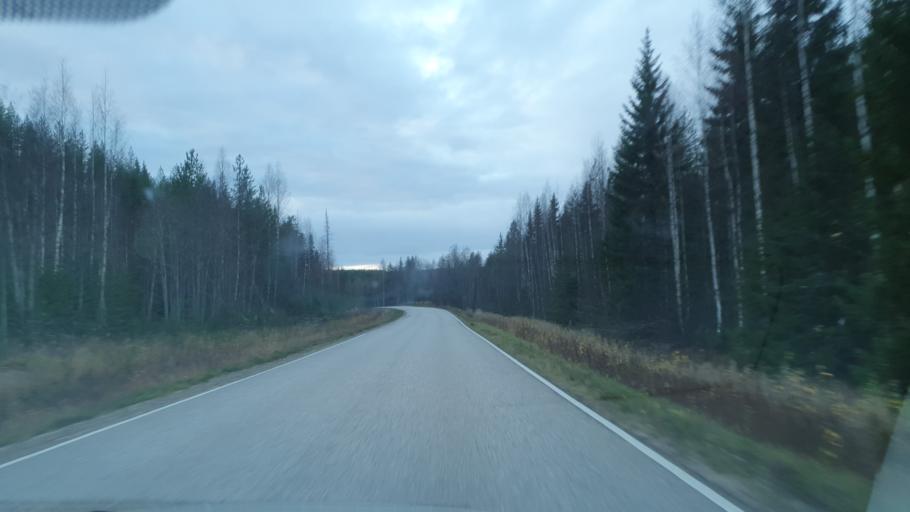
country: FI
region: Kainuu
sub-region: Kajaani
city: Ristijaervi
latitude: 64.4268
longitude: 28.3908
